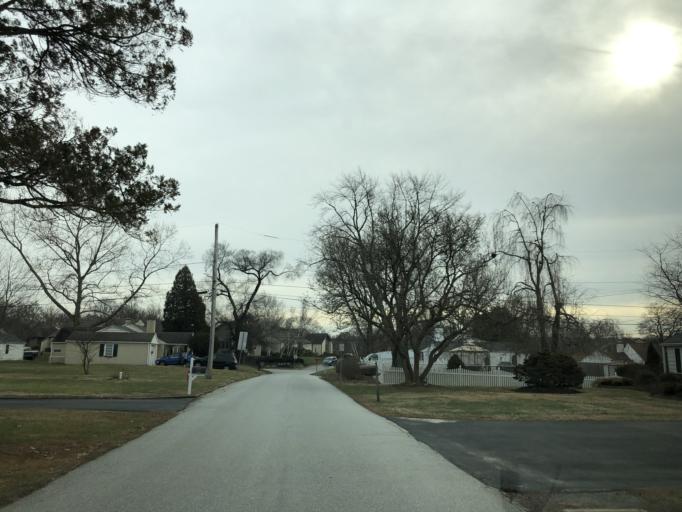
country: US
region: Pennsylvania
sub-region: Chester County
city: Exton
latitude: 40.0351
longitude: -75.6257
